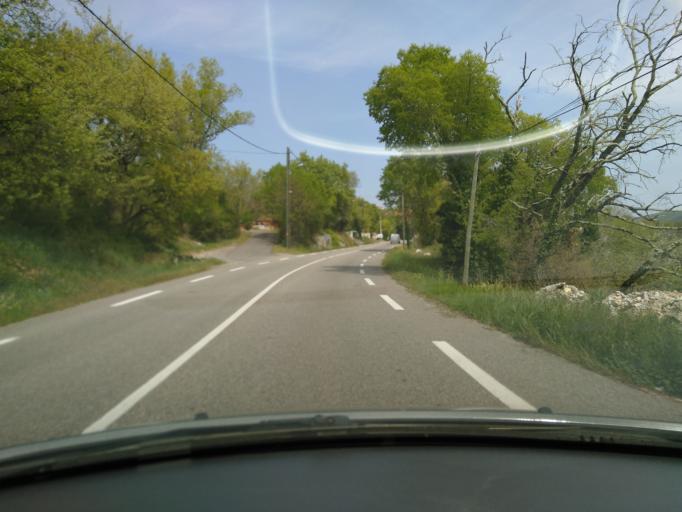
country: FR
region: Rhone-Alpes
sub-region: Departement de l'Ardeche
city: Saint-Sernin
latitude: 44.5433
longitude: 4.4185
